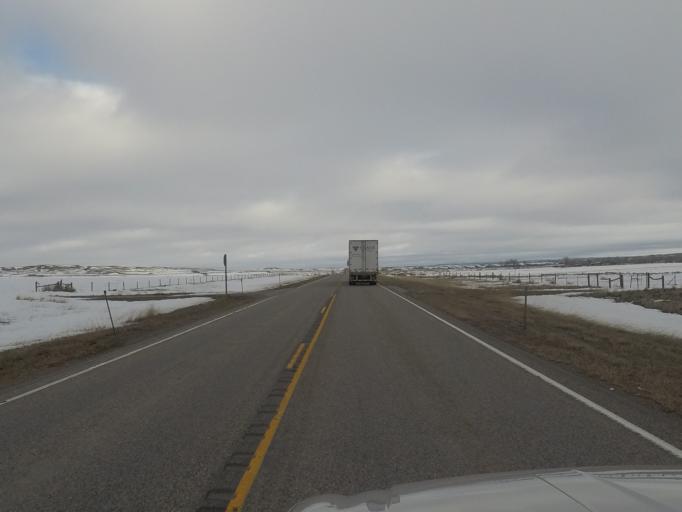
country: US
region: Montana
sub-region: Golden Valley County
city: Ryegate
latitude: 46.3064
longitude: -108.9893
